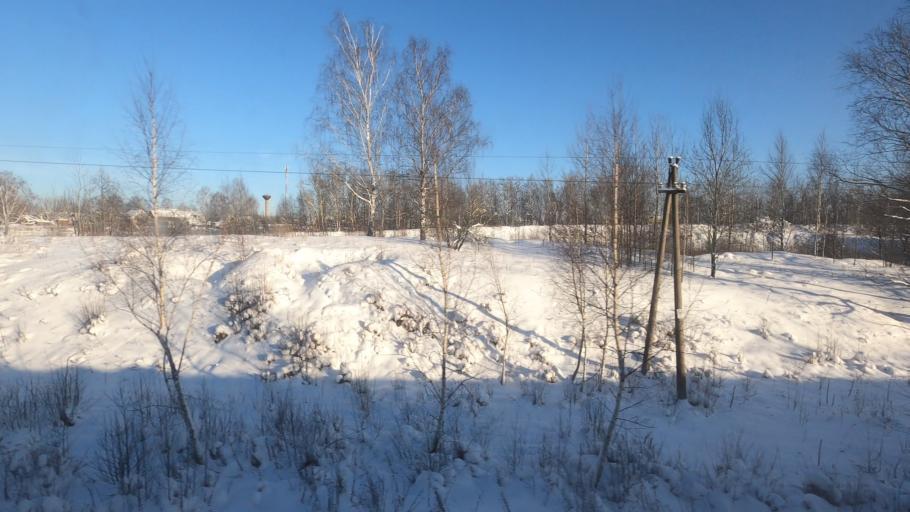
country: RU
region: Moskovskaya
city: Orud'yevo
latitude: 56.3977
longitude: 37.4956
